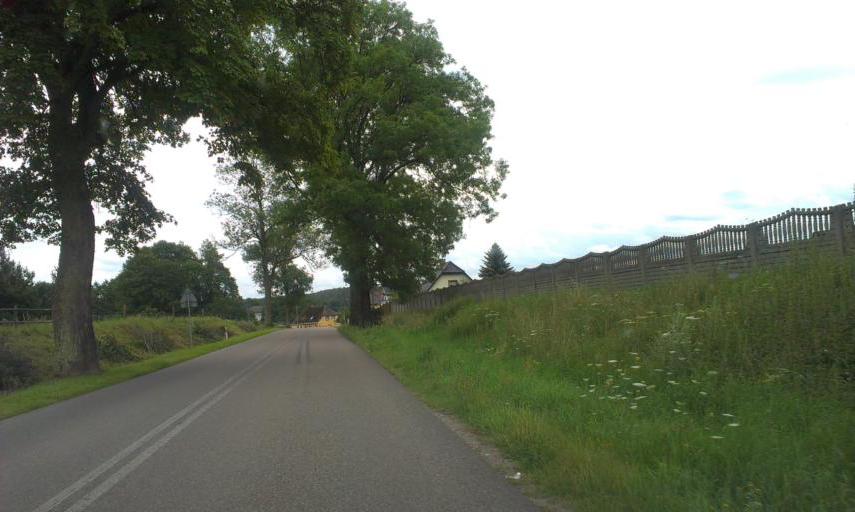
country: PL
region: West Pomeranian Voivodeship
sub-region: Powiat szczecinecki
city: Barwice
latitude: 53.7589
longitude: 16.2424
